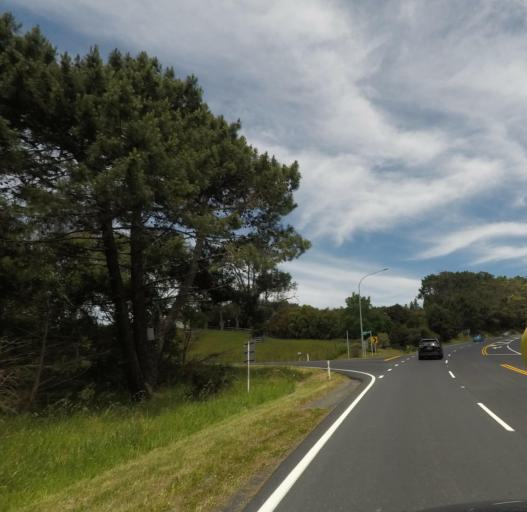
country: NZ
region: Auckland
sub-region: Auckland
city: Rothesay Bay
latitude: -36.6858
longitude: 174.7051
